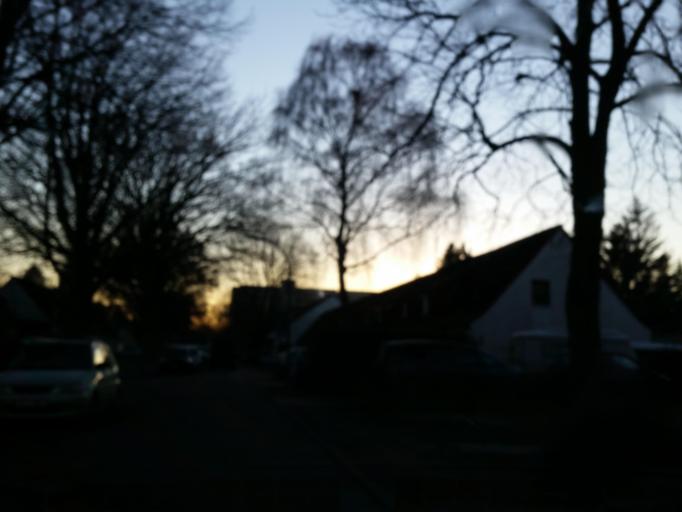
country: DE
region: Hamburg
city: Wandsbek
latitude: 53.5509
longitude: 10.1036
